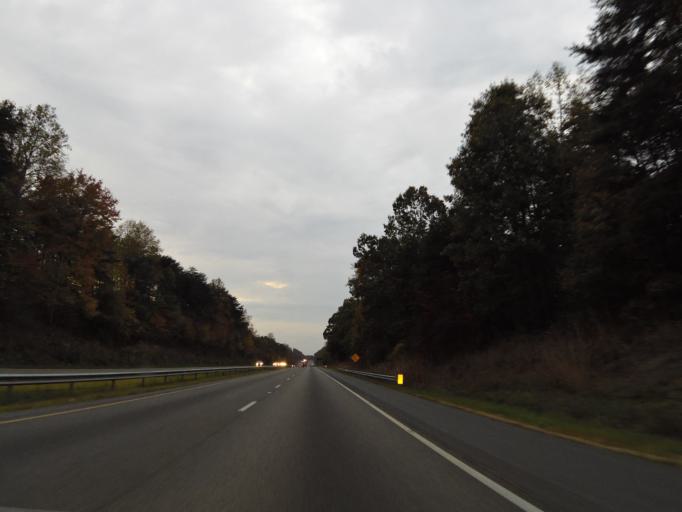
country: US
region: North Carolina
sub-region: Burke County
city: Icard
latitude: 35.7260
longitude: -81.4869
